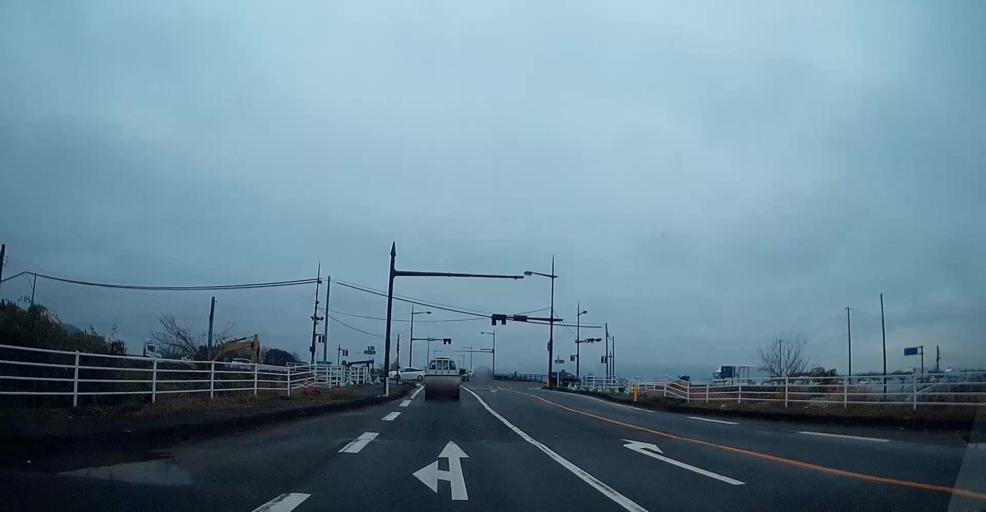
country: JP
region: Kumamoto
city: Kumamoto
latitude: 32.7383
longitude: 130.7403
